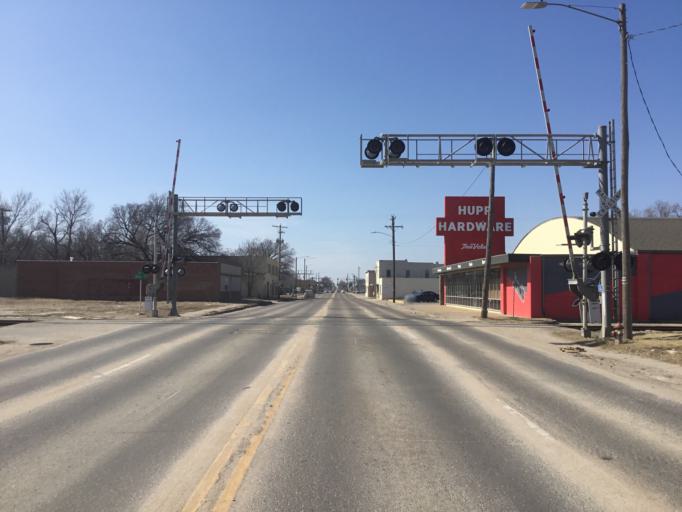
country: US
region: Kansas
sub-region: Sedgwick County
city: Wichita
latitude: 37.6644
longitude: -97.3287
